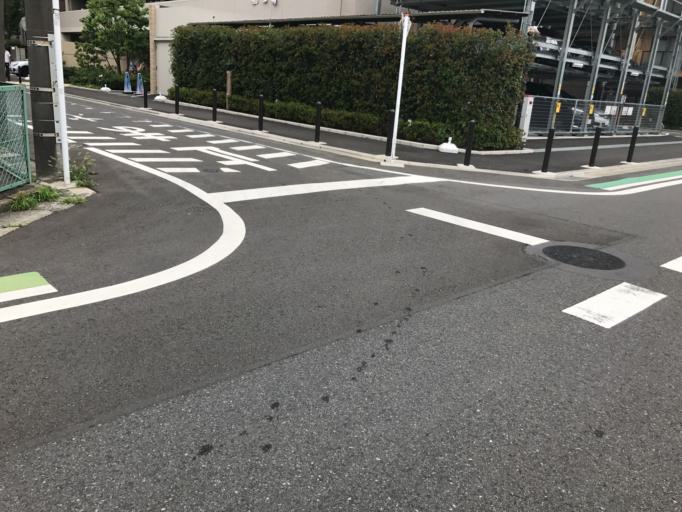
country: JP
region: Tokyo
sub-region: Machida-shi
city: Machida
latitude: 35.5781
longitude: 139.3769
